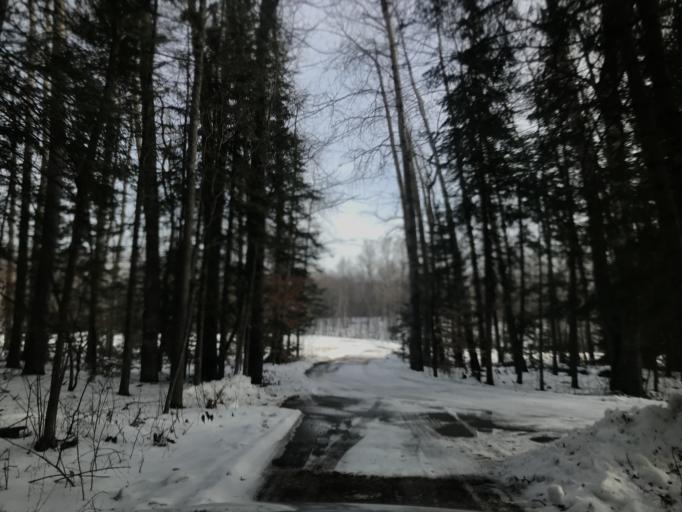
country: US
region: Wisconsin
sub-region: Door County
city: Sturgeon Bay
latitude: 45.1516
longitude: -87.0563
